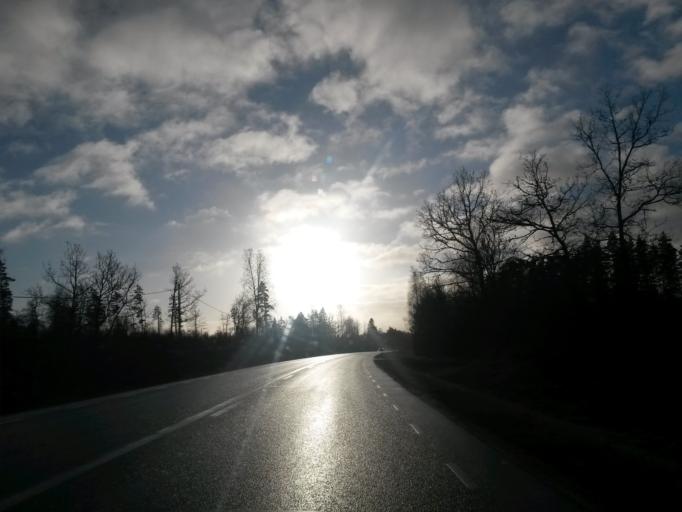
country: SE
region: Vaestra Goetaland
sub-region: Vargarda Kommun
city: Vargarda
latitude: 58.0120
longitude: 12.8181
